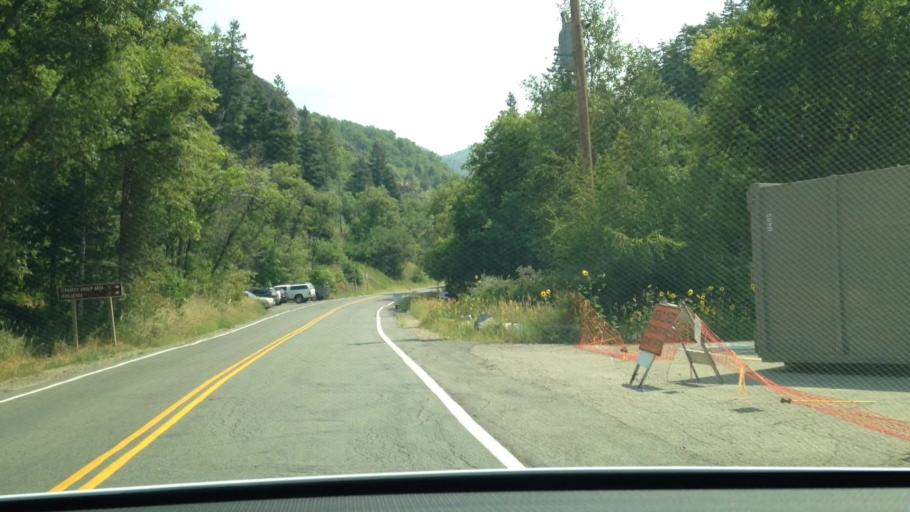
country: US
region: Utah
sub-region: Salt Lake County
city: Mount Olympus
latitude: 40.6998
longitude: -111.7174
